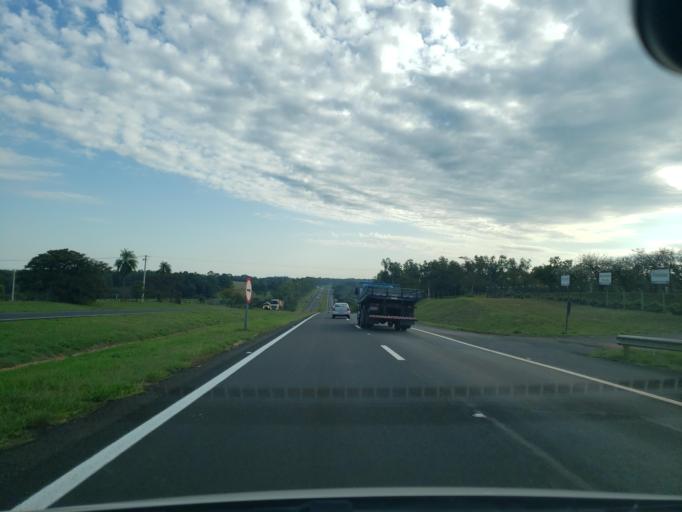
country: BR
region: Sao Paulo
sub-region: Guararapes
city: Guararapes
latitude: -21.2099
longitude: -50.6681
